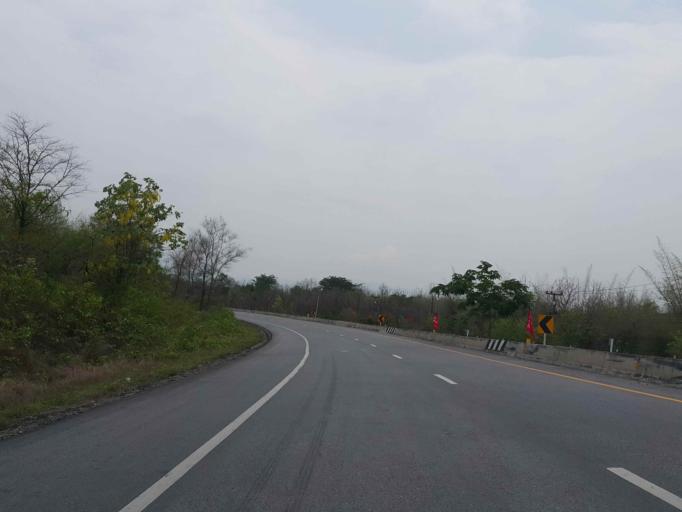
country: TH
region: Lampang
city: Sop Prap
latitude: 17.9696
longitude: 99.3528
